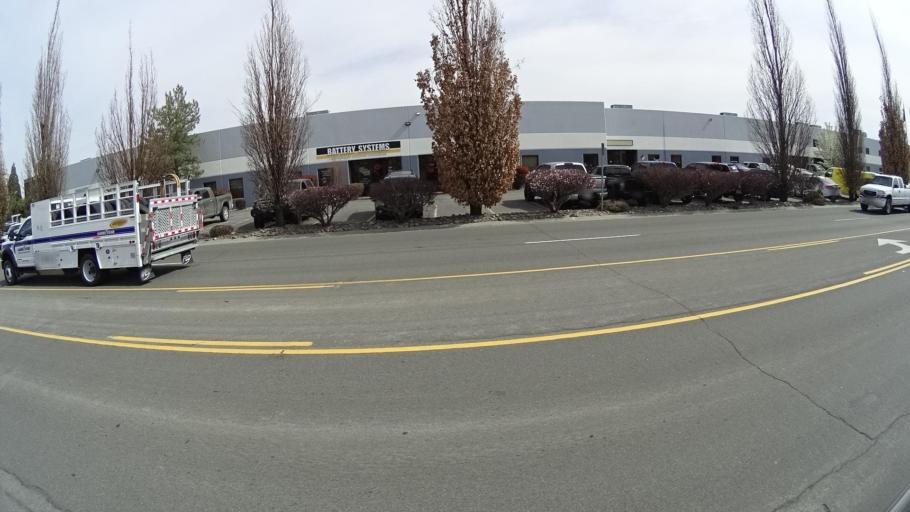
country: US
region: Nevada
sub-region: Washoe County
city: Sparks
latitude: 39.5225
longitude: -119.7565
